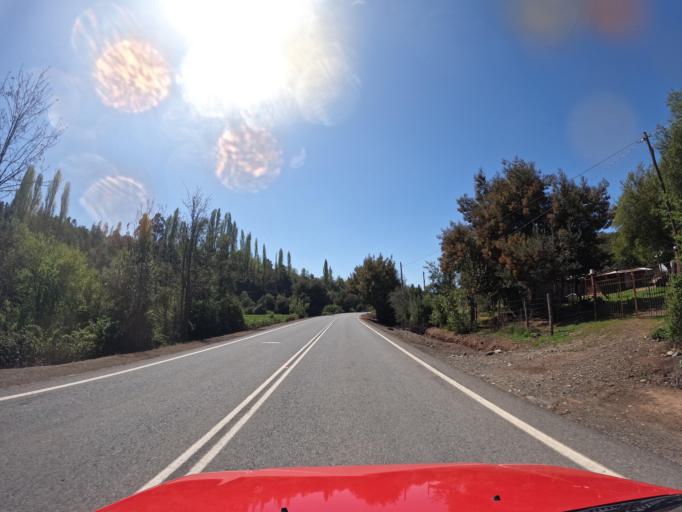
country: CL
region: Maule
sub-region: Provincia de Talca
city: San Clemente
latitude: -35.4591
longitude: -71.2697
